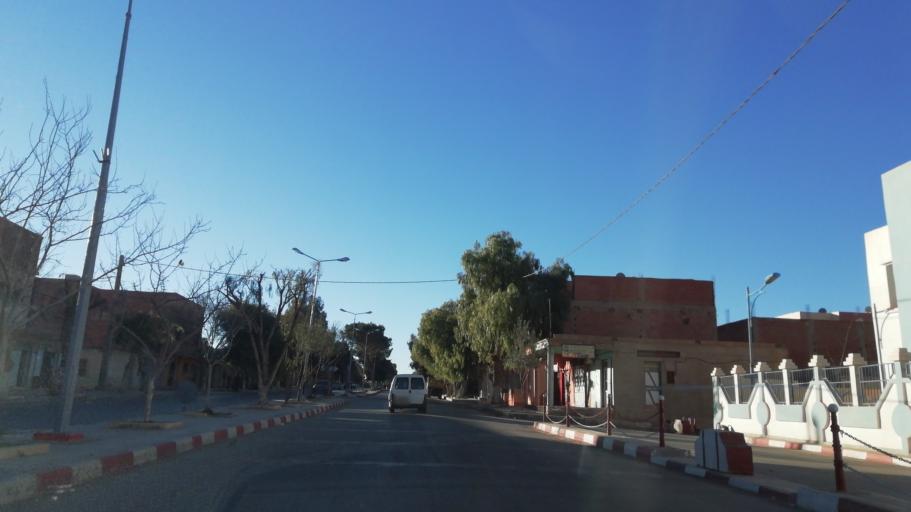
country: DZ
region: Saida
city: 'Ain el Hadjar
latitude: 34.0390
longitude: 0.0872
